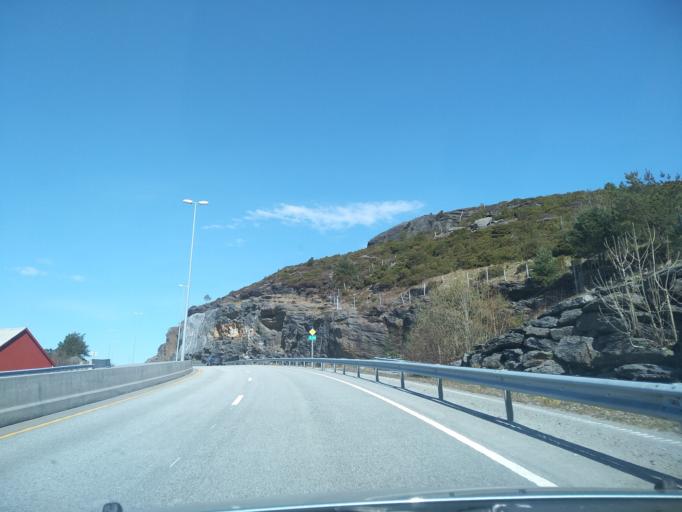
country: NO
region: Rogaland
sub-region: Tysvaer
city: Tysvaer
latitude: 59.2803
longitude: 5.4783
